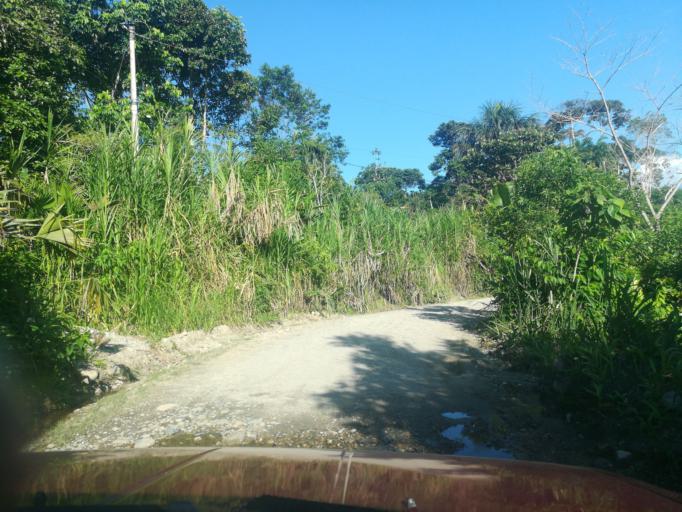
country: EC
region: Napo
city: Tena
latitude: -0.9923
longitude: -77.8278
